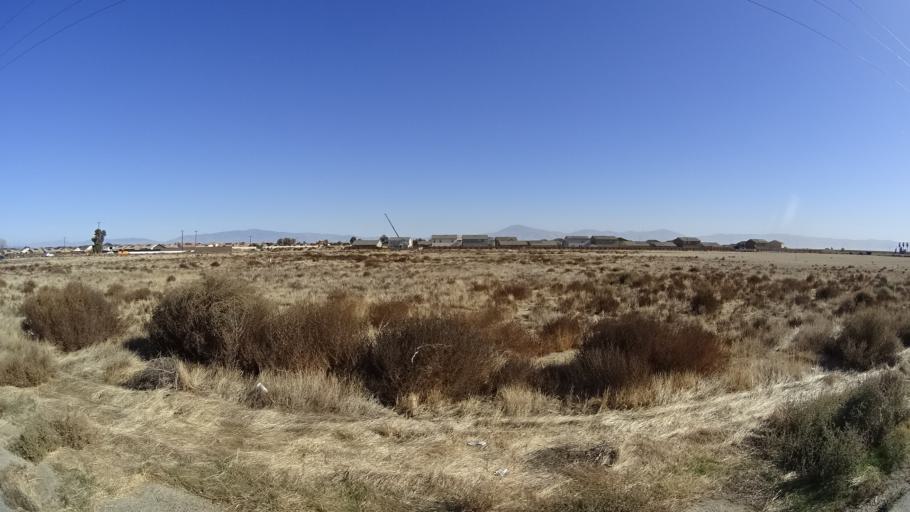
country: US
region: California
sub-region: Kern County
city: Greenfield
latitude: 35.2655
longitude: -119.0746
